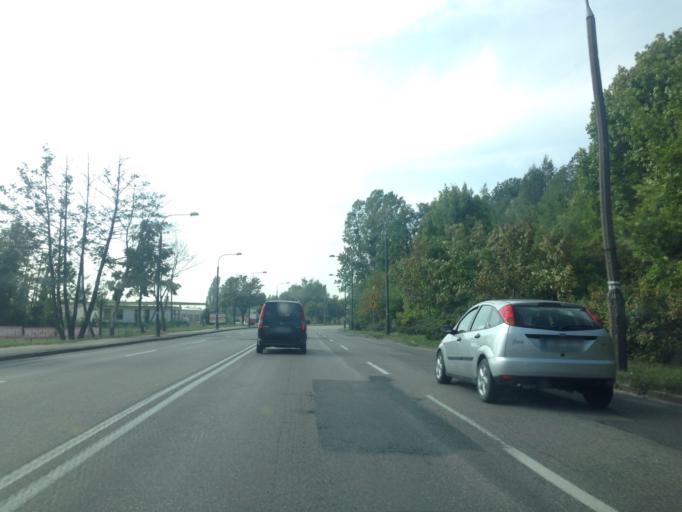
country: PL
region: Kujawsko-Pomorskie
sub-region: Powiat brodnicki
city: Brodnica
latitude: 53.2674
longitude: 19.4117
